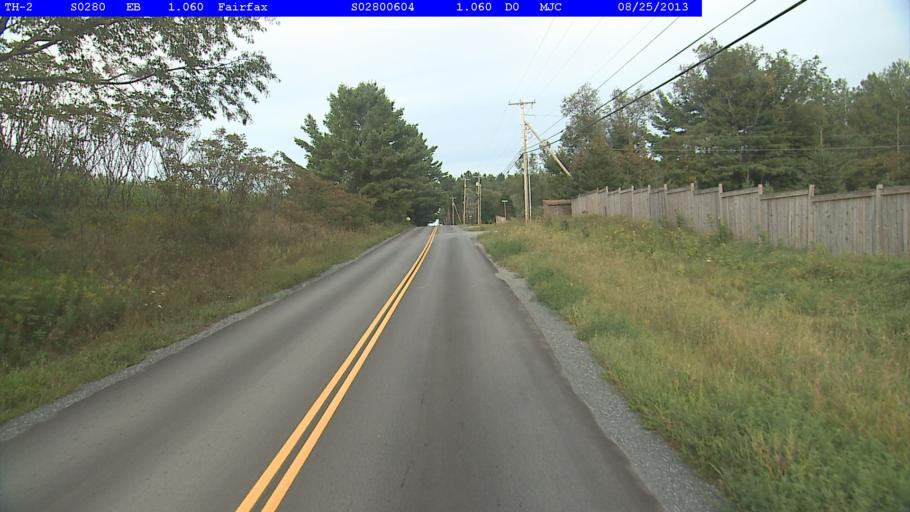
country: US
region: Vermont
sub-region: Chittenden County
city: Milton
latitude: 44.6701
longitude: -72.9908
